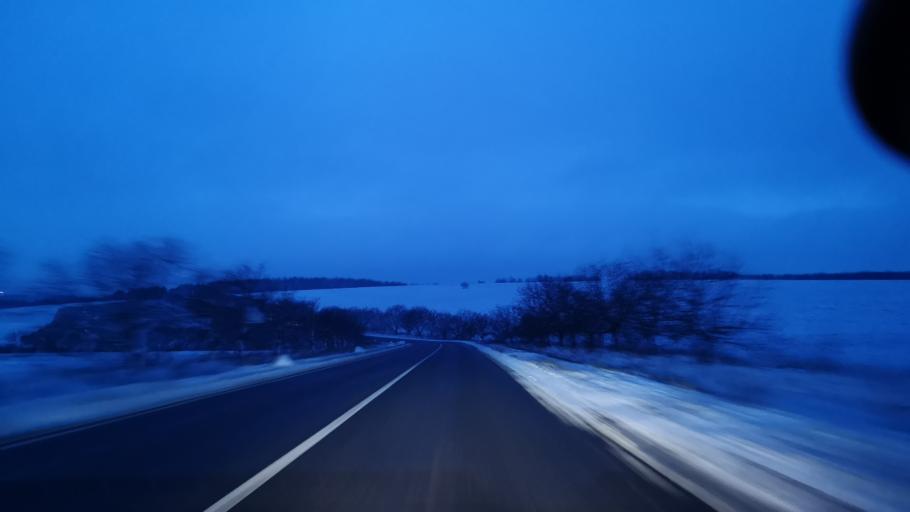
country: MD
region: Orhei
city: Orhei
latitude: 47.5740
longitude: 28.7997
